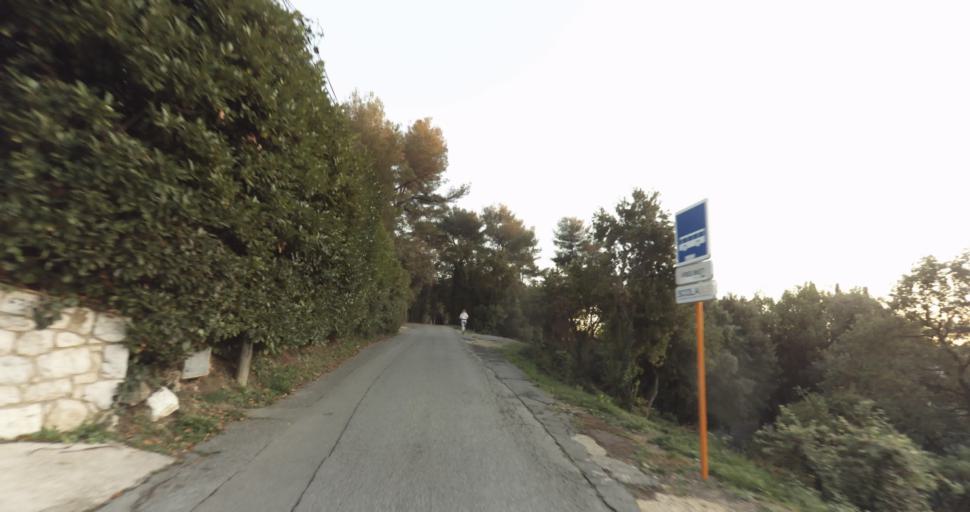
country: FR
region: Provence-Alpes-Cote d'Azur
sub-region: Departement des Alpes-Maritimes
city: La Gaude
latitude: 43.7304
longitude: 7.1333
